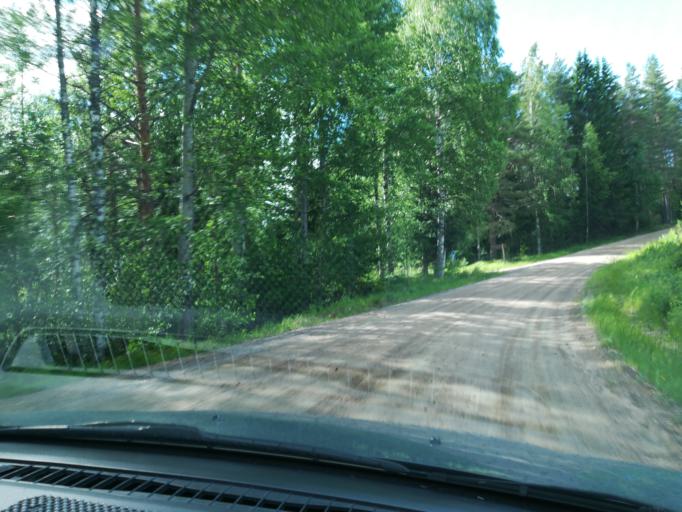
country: FI
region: South Karelia
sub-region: Lappeenranta
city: Savitaipale
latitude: 61.3012
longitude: 27.6381
